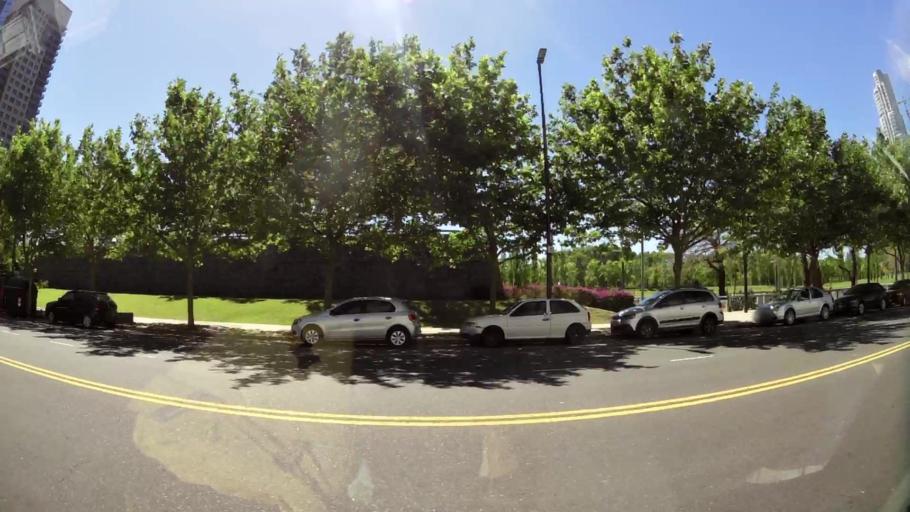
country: AR
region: Buenos Aires F.D.
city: Buenos Aires
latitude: -34.6075
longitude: -58.3630
